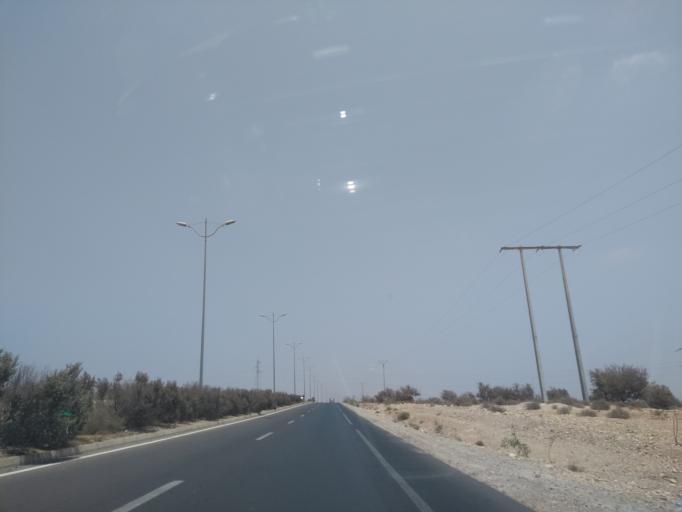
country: MA
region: Souss-Massa-Draa
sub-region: Inezgane-Ait Mellou
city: Inezgane
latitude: 30.4091
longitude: -9.4196
